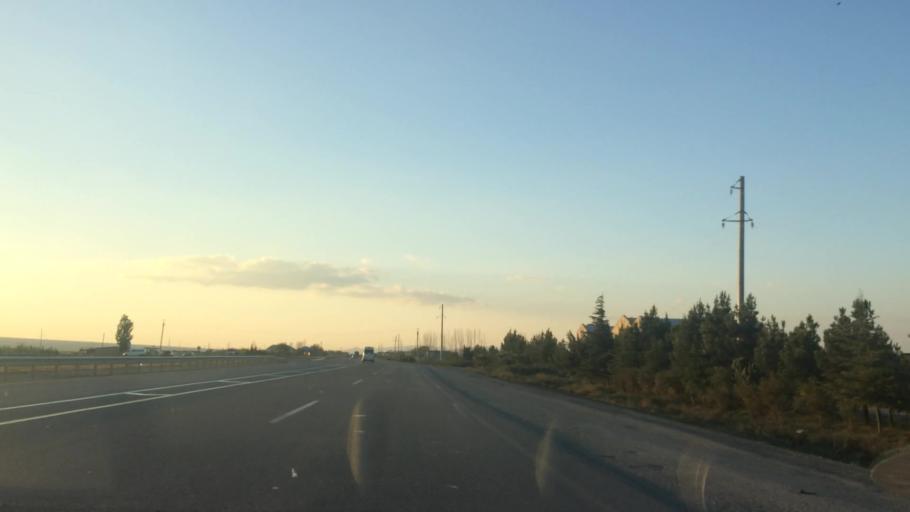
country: AZ
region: Haciqabul
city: Haciqabul
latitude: 40.0069
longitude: 49.1593
